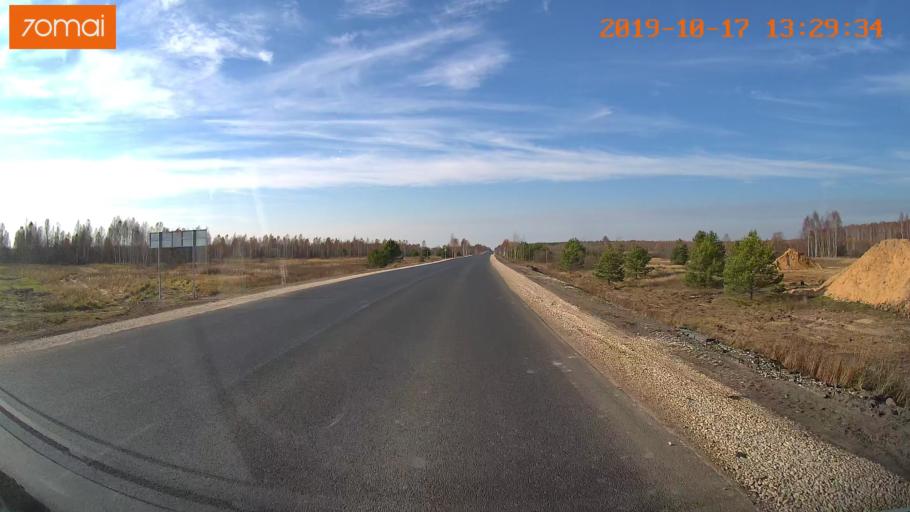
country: RU
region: Vladimir
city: Velikodvorskiy
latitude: 55.1199
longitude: 40.8376
